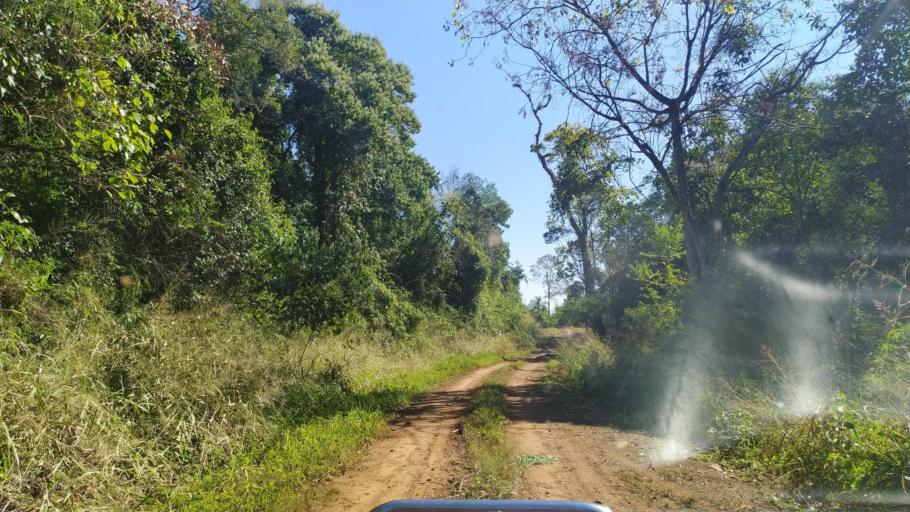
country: AR
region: Misiones
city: El Alcazar
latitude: -26.7590
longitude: -54.5802
